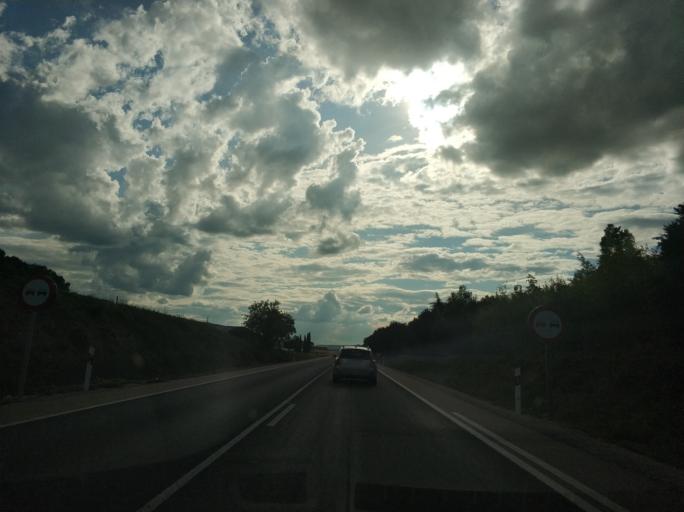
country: ES
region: Castille and Leon
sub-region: Provincia de Valladolid
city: Valbuena de Duero
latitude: 41.6286
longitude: -4.2954
